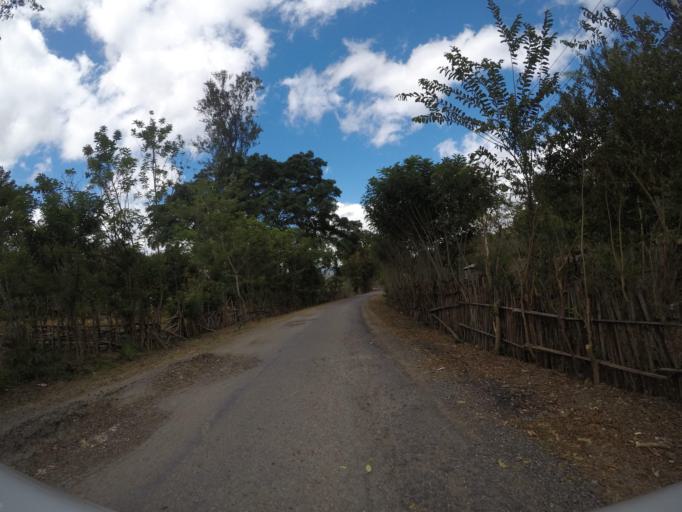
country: TL
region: Lautem
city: Lospalos
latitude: -8.4558
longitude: 126.8220
